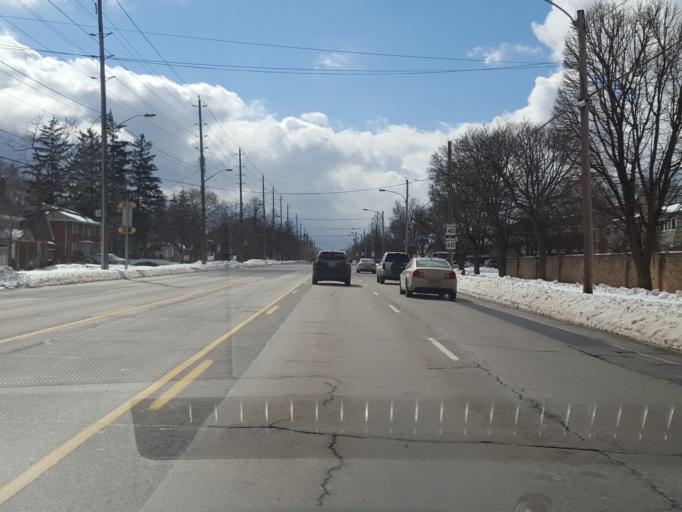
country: CA
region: Ontario
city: Hamilton
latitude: 43.3125
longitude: -79.8452
